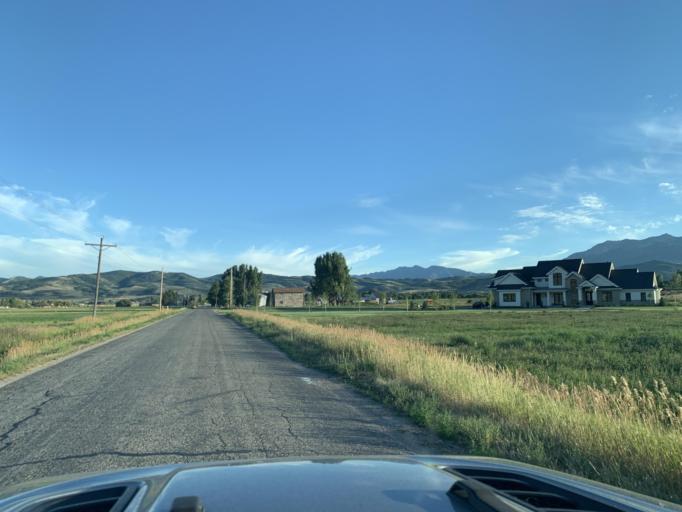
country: US
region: Utah
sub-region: Weber County
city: Wolf Creek
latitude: 41.2731
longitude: -111.7619
